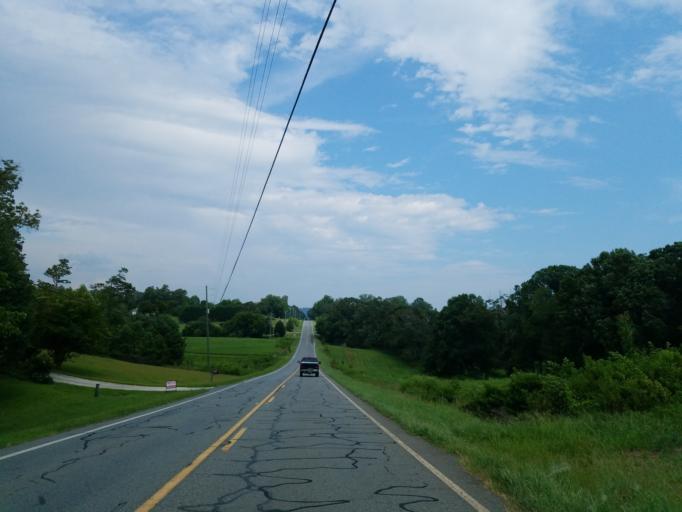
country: US
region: Georgia
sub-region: Gilmer County
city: Ellijay
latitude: 34.6437
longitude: -84.5507
